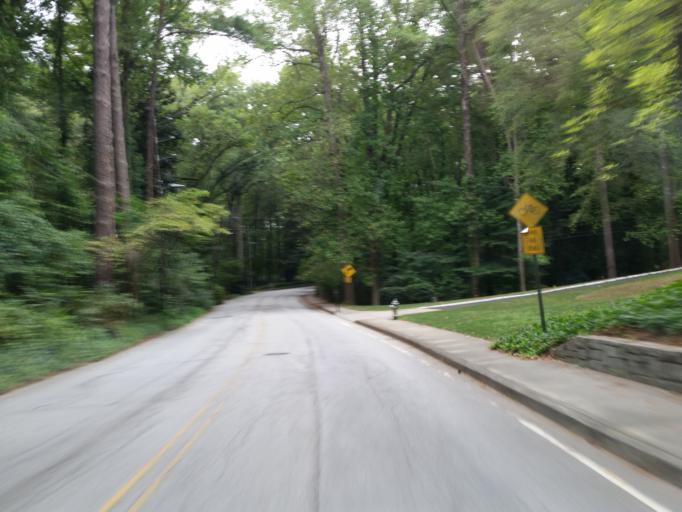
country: US
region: Georgia
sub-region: Cobb County
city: Vinings
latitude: 33.8330
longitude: -84.4184
